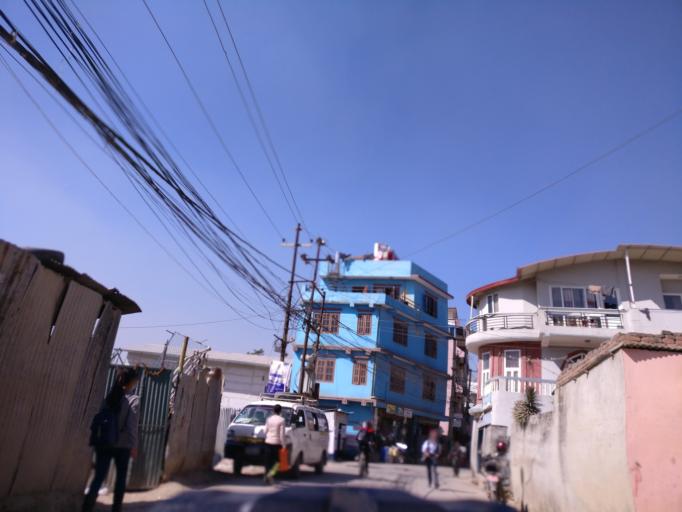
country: NP
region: Central Region
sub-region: Bagmati Zone
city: Patan
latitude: 27.6721
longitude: 85.3446
